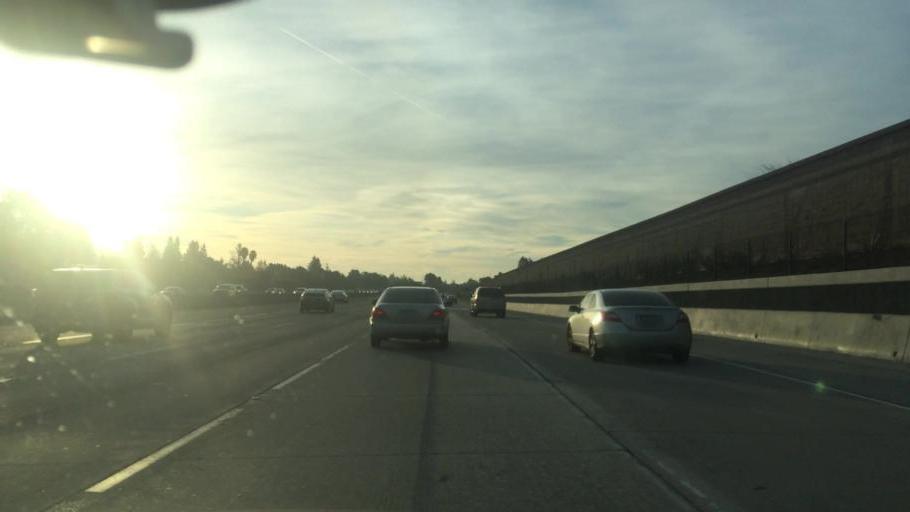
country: US
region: California
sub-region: Contra Costa County
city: San Ramon
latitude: 37.7989
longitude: -121.9874
